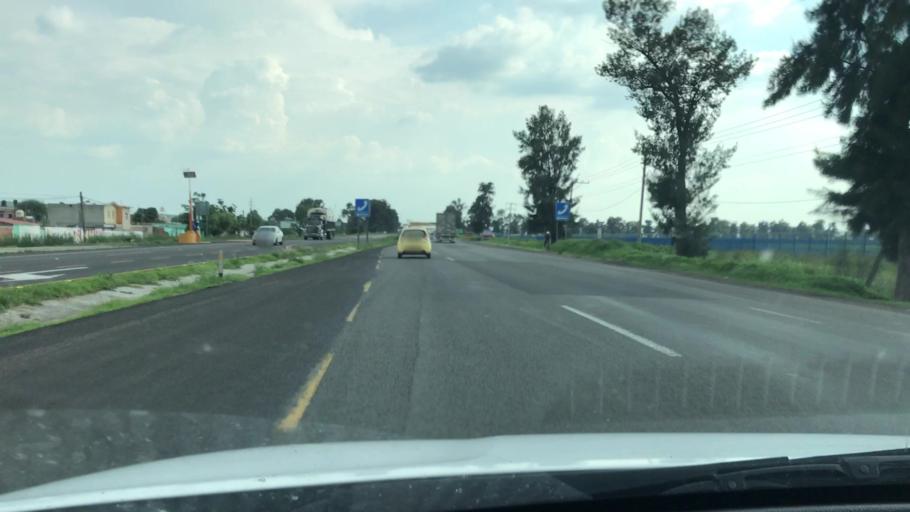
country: MX
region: Guanajuato
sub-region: Irapuato
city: Colonia Morelos de Guadalupe de Rivera
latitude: 20.6026
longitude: -101.4153
